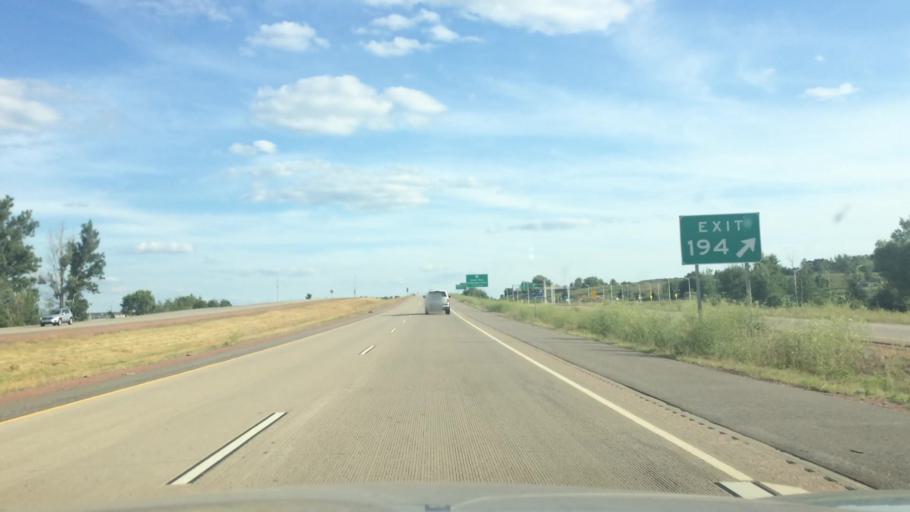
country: US
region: Wisconsin
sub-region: Marathon County
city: Wausau
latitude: 44.9950
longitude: -89.6576
